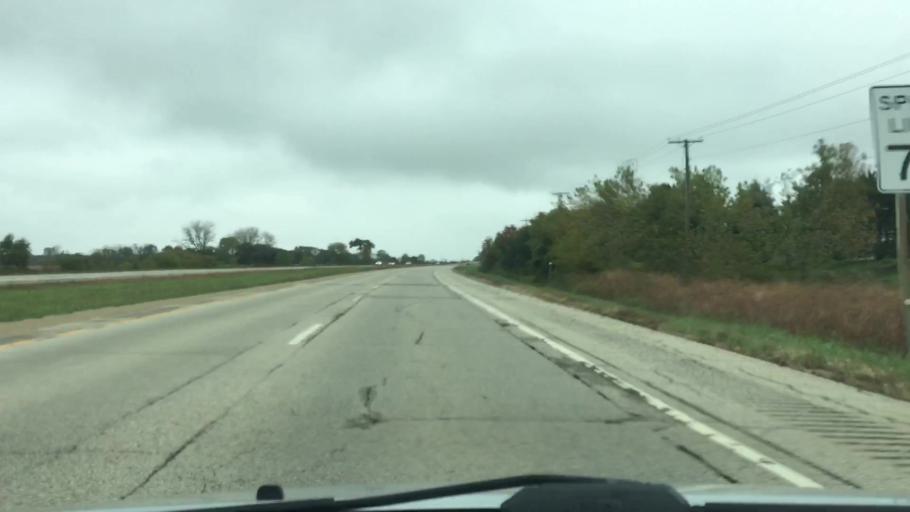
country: US
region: Wisconsin
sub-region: Walworth County
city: Elkhorn
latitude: 42.6913
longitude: -88.5348
